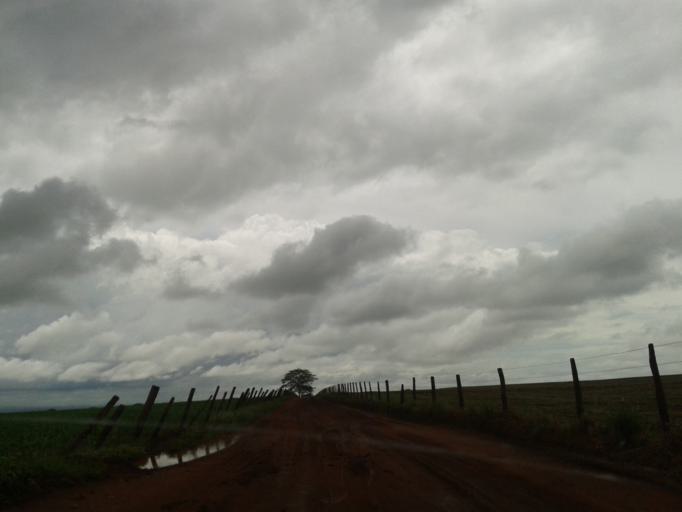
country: BR
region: Minas Gerais
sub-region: Santa Vitoria
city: Santa Vitoria
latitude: -18.6666
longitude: -49.9221
